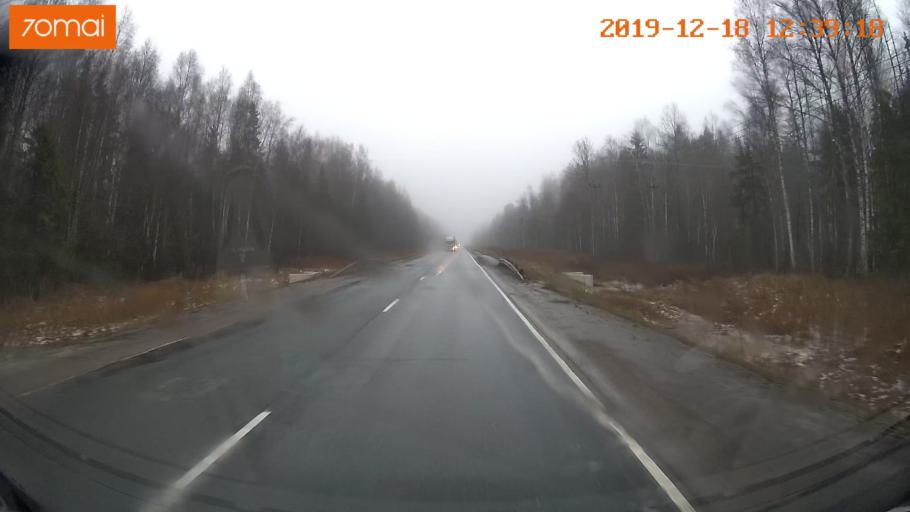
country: RU
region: Moskovskaya
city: Vysokovsk
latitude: 56.1631
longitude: 36.6105
